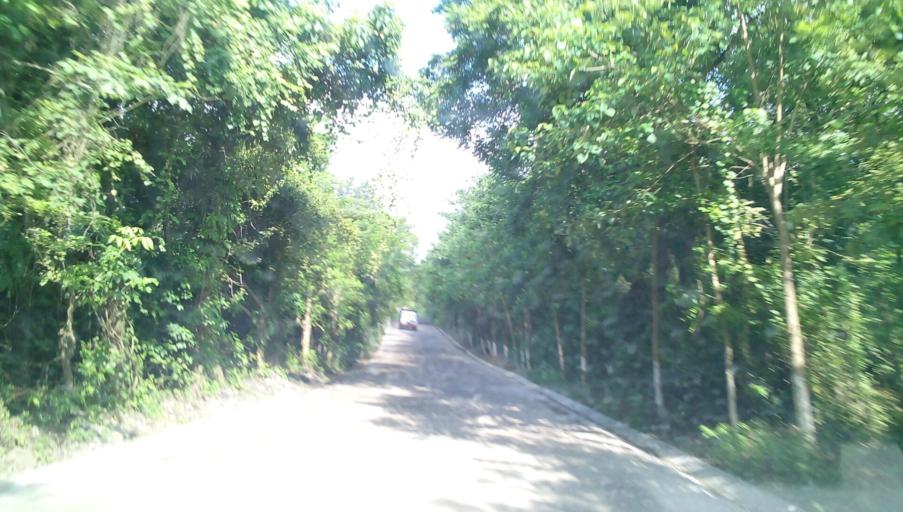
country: MX
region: Veracruz
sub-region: Citlaltepetl
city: Las Sabinas
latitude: 21.3401
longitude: -97.8847
